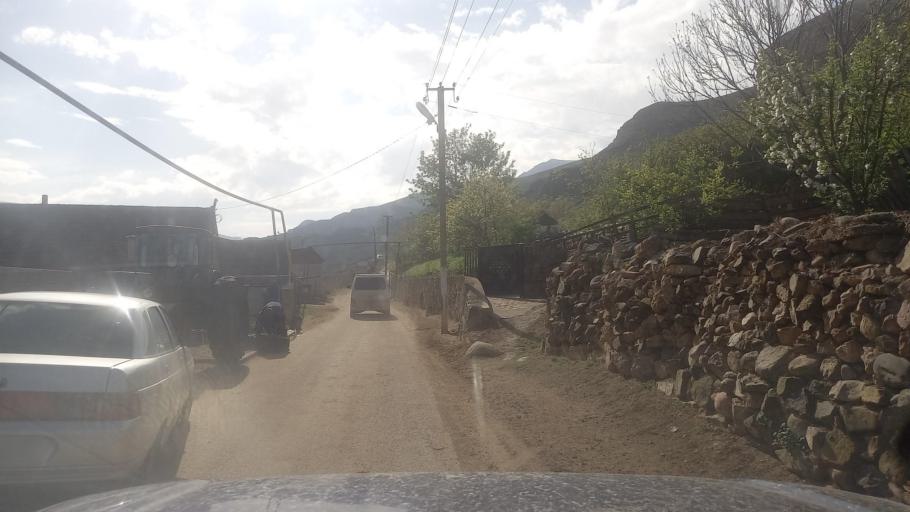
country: RU
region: Kabardino-Balkariya
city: Kamennomostskoye
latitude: 43.7256
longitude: 42.9140
